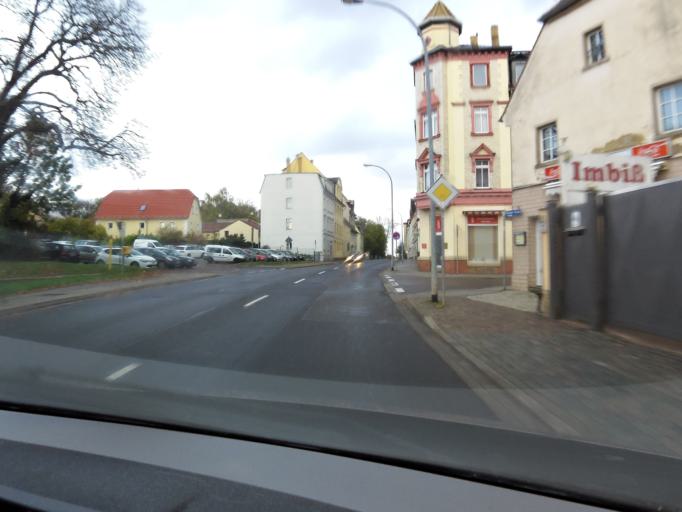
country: DE
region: Saxony
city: Markkleeberg
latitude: 51.2791
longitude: 12.3594
